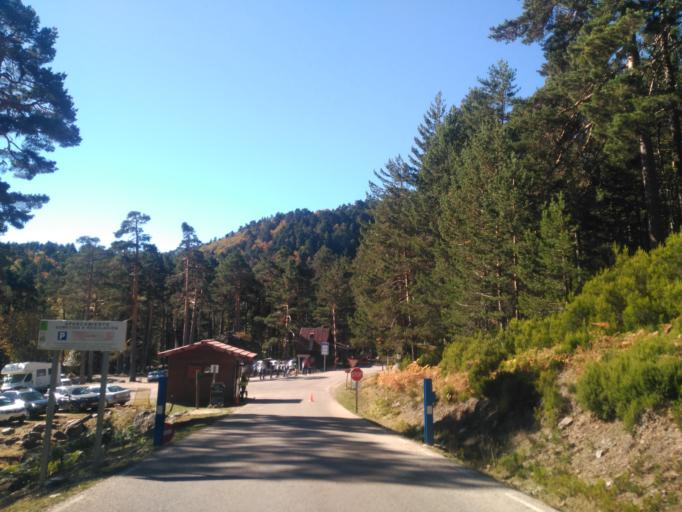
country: ES
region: Castille and Leon
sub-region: Provincia de Soria
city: Covaleda
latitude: 41.9989
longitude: -2.8268
